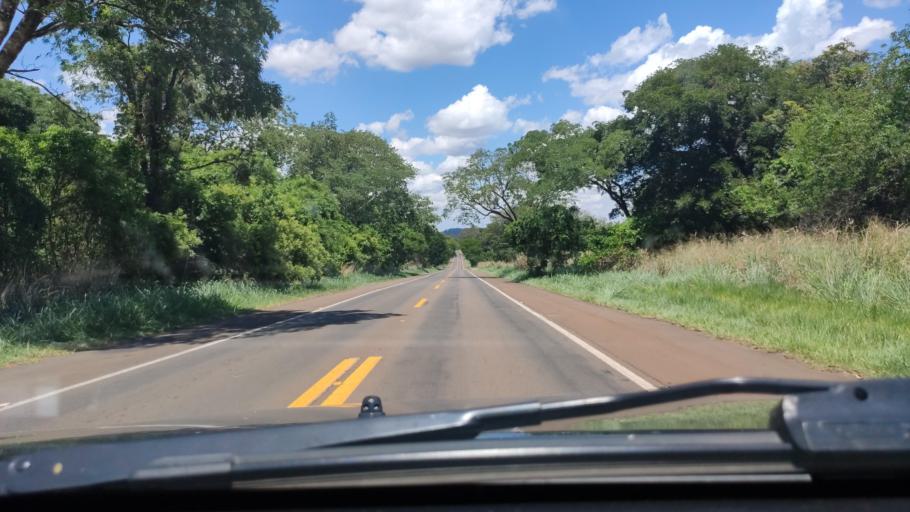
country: BR
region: Sao Paulo
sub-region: Boa Esperanca Do Sul
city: Boa Esperanca do Sul
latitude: -22.0696
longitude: -48.4129
